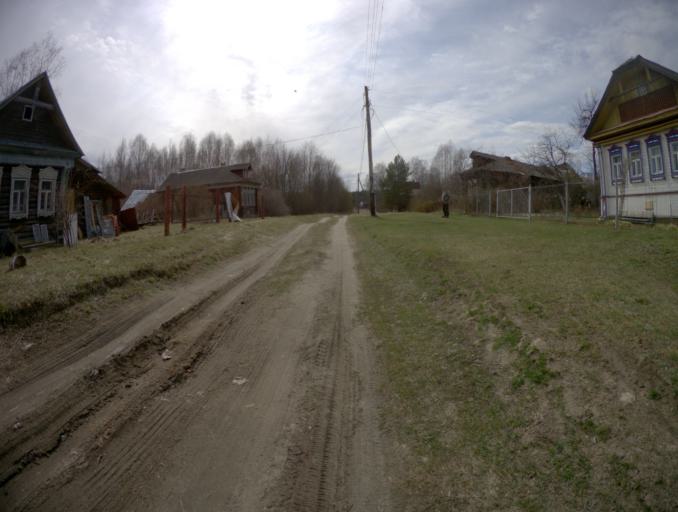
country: RU
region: Vladimir
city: Raduzhnyy
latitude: 55.8697
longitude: 40.2078
